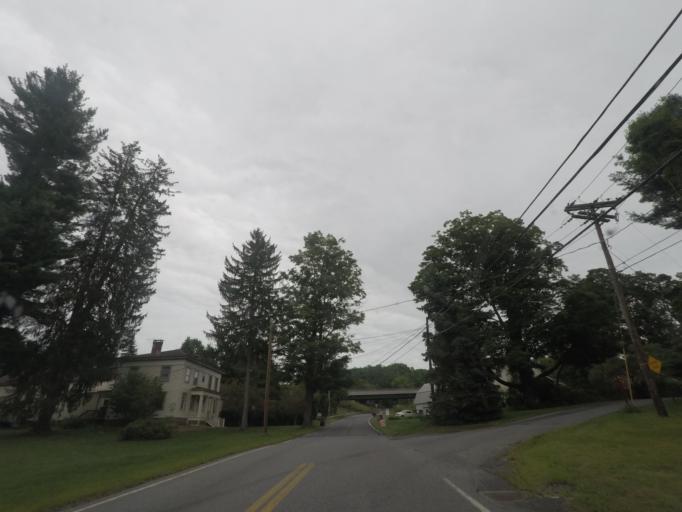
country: US
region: New York
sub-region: Columbia County
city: Chatham
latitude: 42.4407
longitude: -73.5577
